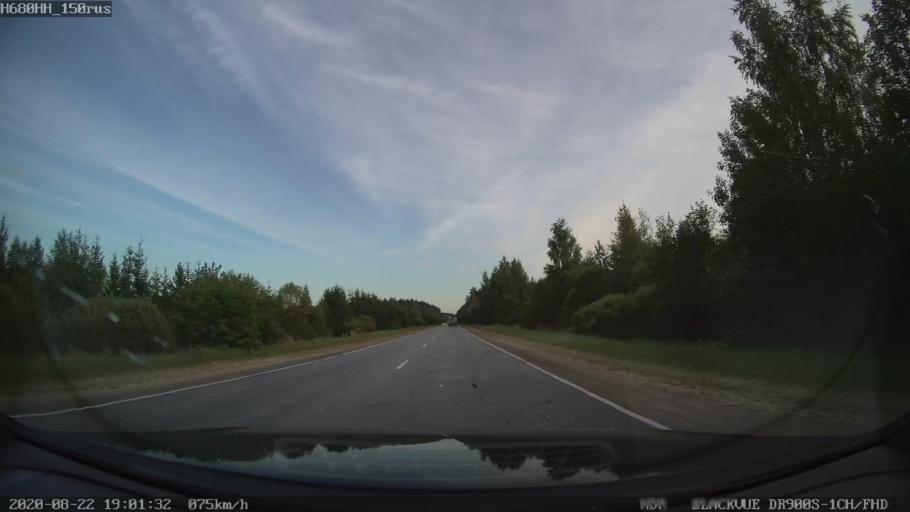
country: RU
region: Tverskaya
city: Vasil'yevskiy Mokh
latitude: 57.1182
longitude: 36.1155
